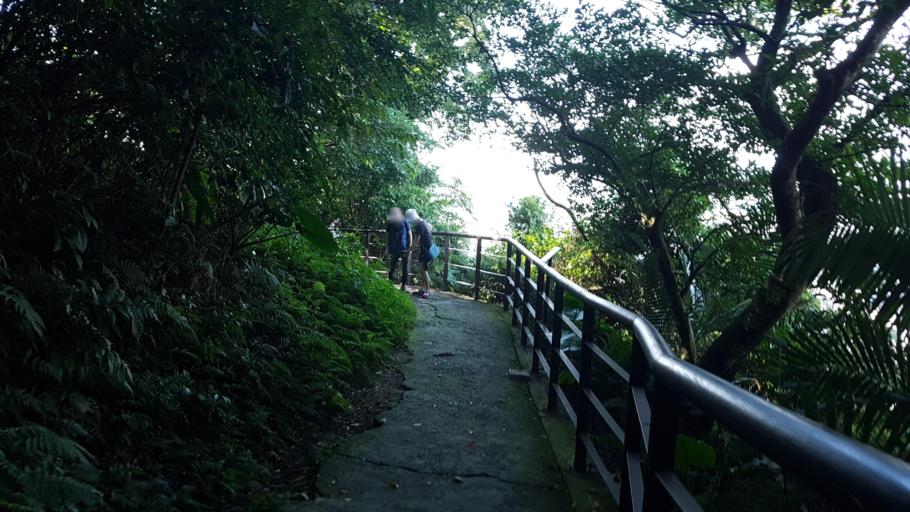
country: TW
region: Taipei
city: Taipei
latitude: 24.9929
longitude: 121.5492
